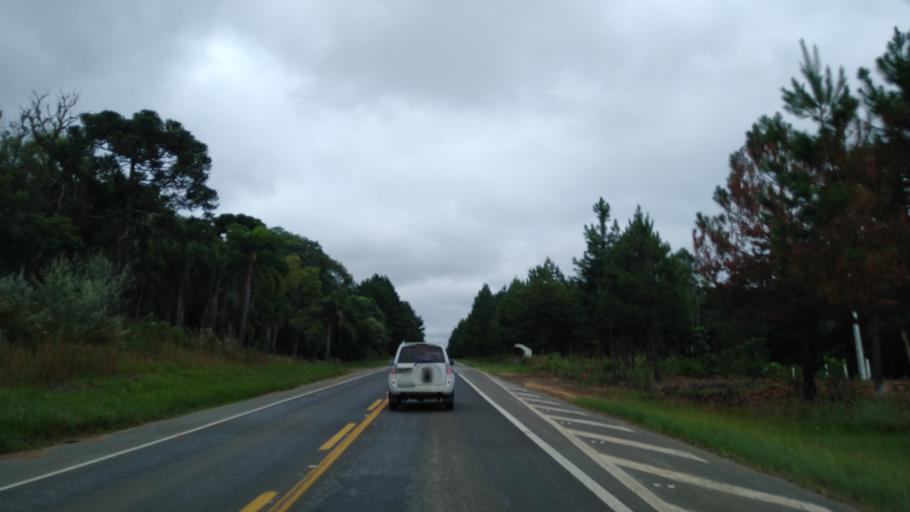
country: BR
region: Santa Catarina
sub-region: Tres Barras
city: Tres Barras
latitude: -26.1803
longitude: -50.1945
